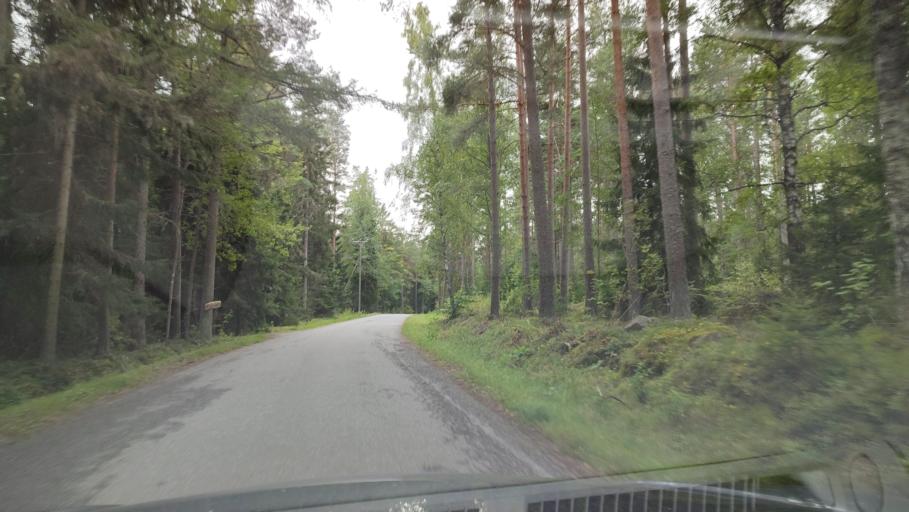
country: FI
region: Ostrobothnia
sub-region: Sydosterbotten
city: Kristinestad
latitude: 62.2525
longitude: 21.3538
